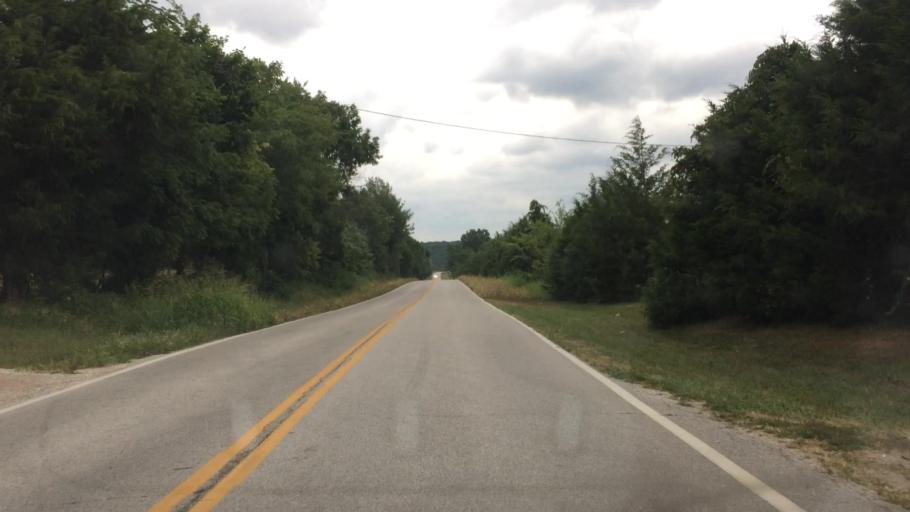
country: US
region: Missouri
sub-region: Greene County
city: Strafford
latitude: 37.2860
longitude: -93.0996
